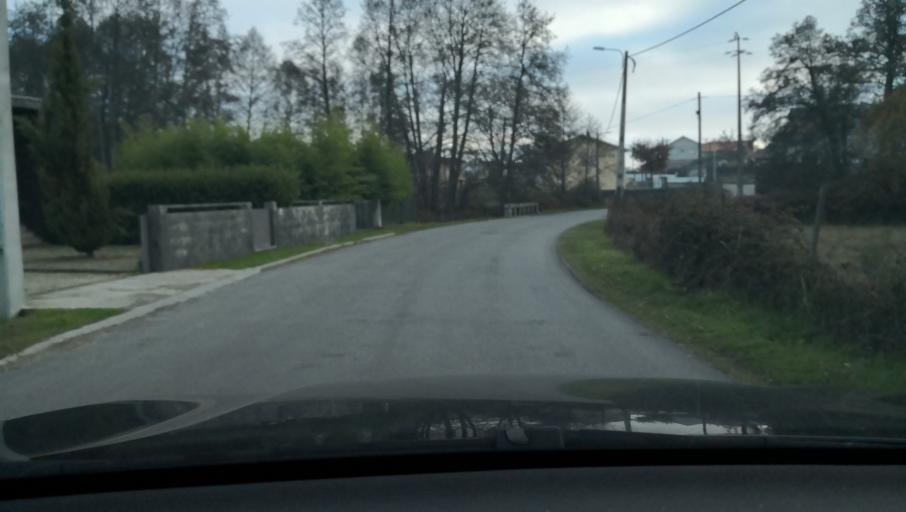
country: PT
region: Vila Real
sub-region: Vila Real
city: Vila Real
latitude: 41.3414
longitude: -7.6630
